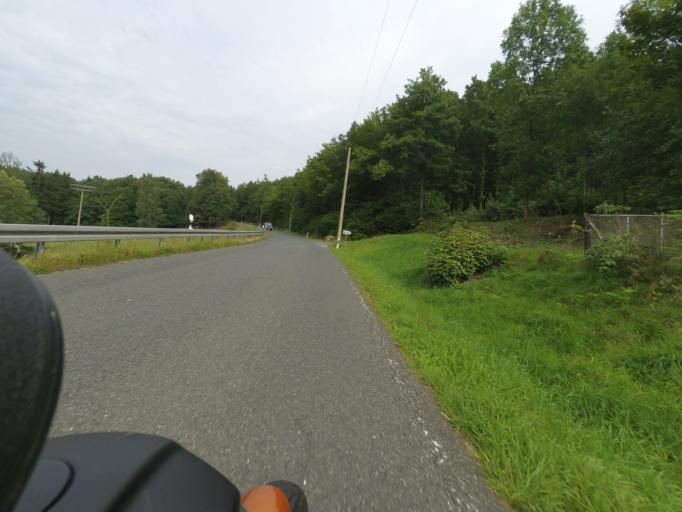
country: DE
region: Saxony
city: Dohna
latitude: 50.9252
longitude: 13.8429
